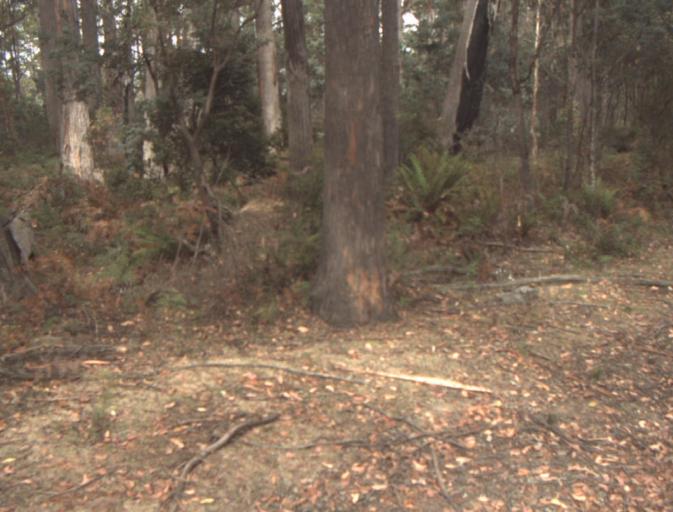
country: AU
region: Tasmania
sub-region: Northern Midlands
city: Evandale
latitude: -41.4956
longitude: 147.5633
